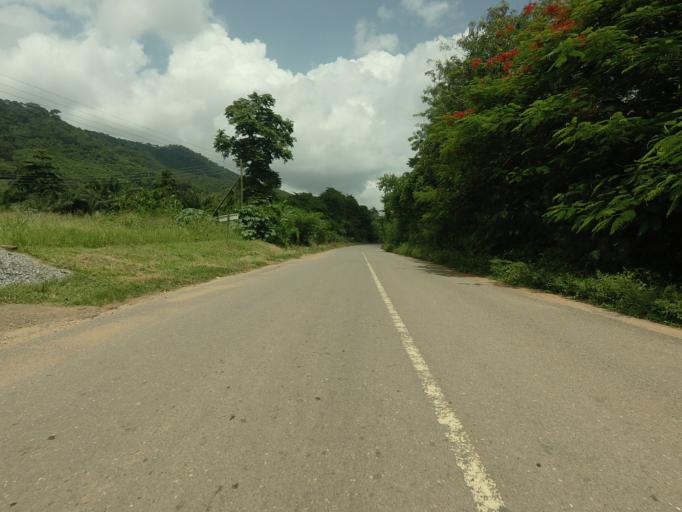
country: GH
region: Volta
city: Ho
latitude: 6.7222
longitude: 0.3414
